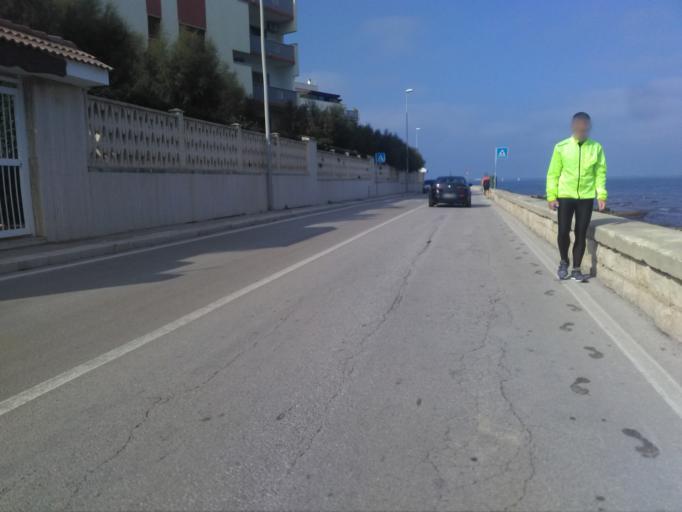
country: IT
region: Apulia
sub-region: Provincia di Bari
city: San Paolo
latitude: 41.1617
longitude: 16.7620
